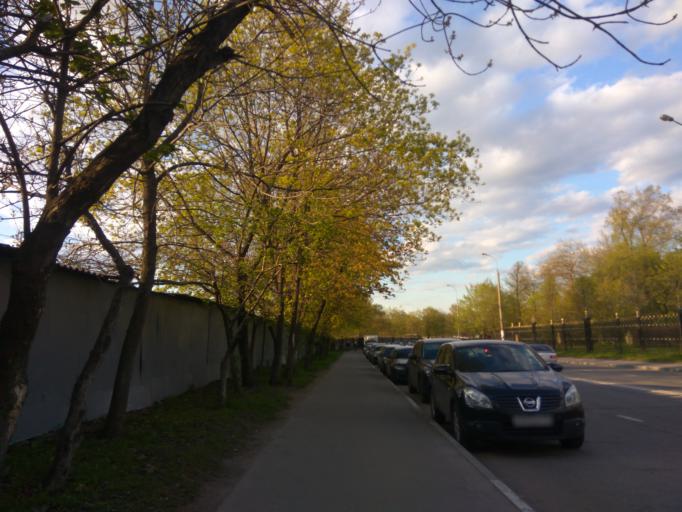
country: RU
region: Moscow
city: Orekhovo-Borisovo Severnoye
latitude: 55.6209
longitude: 37.6741
